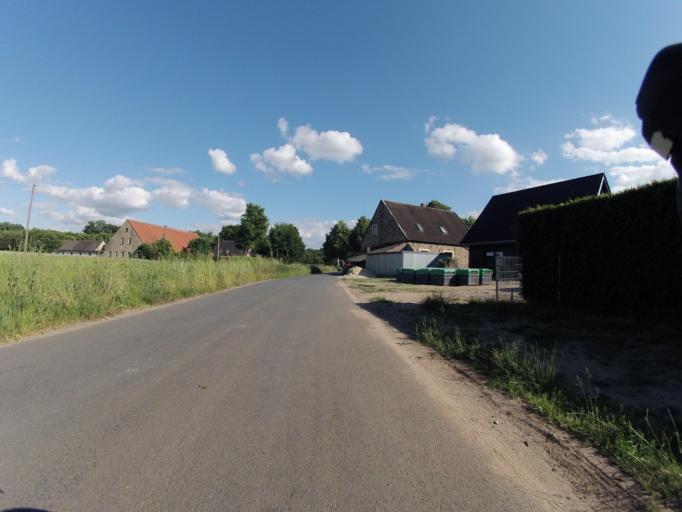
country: DE
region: North Rhine-Westphalia
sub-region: Regierungsbezirk Munster
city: Horstel
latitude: 52.3029
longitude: 7.5925
